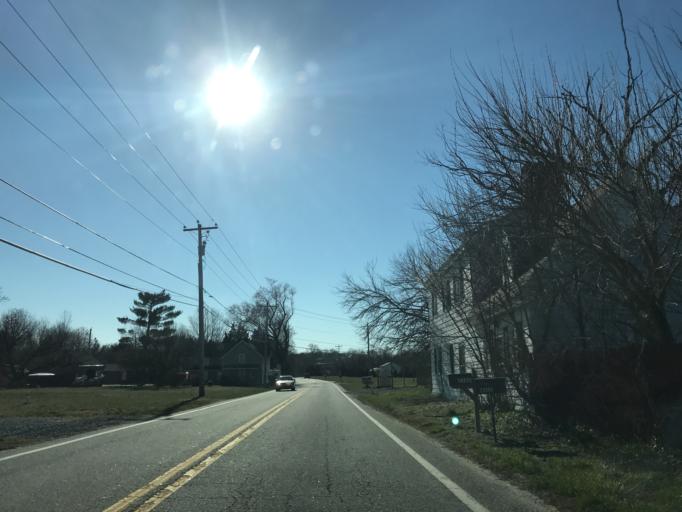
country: US
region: Maryland
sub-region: Caroline County
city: Ridgely
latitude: 39.0343
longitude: -75.8761
